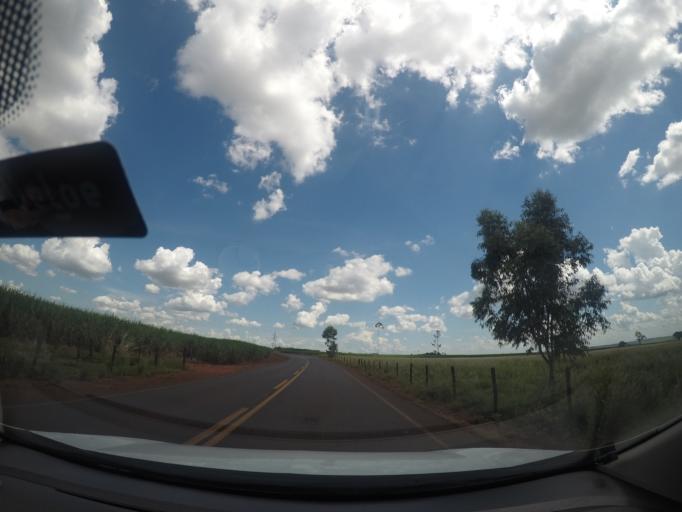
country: BR
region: Minas Gerais
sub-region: Frutal
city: Frutal
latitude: -19.8442
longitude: -48.7375
